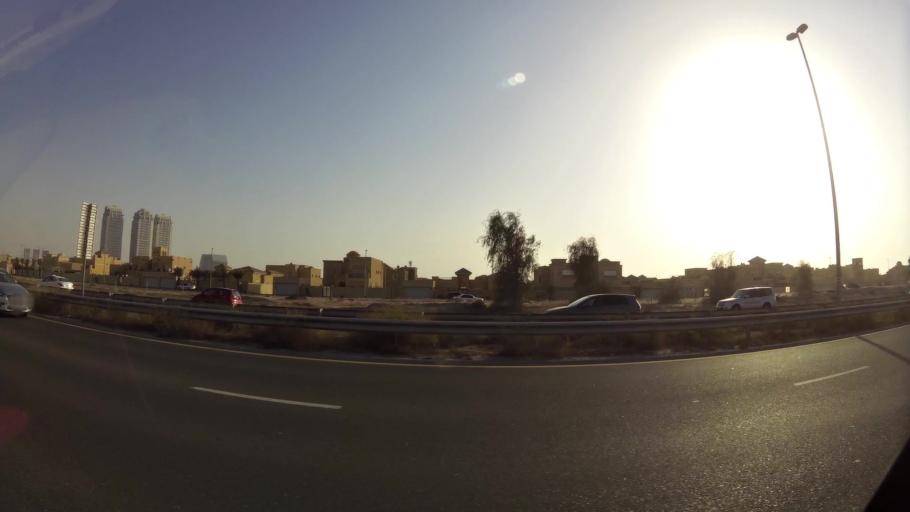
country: AE
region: Dubai
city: Dubai
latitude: 25.0857
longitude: 55.2487
